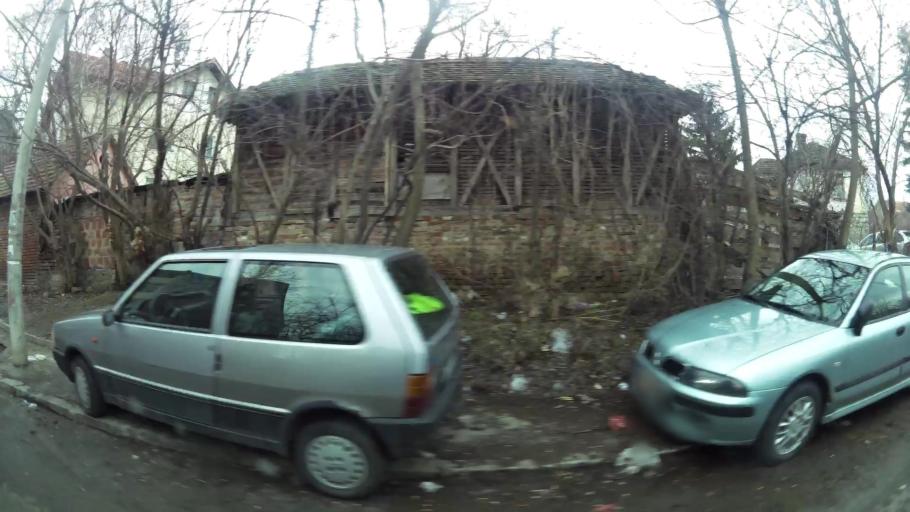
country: RS
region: Central Serbia
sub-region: Belgrade
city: Cukarica
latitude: 44.7596
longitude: 20.4055
